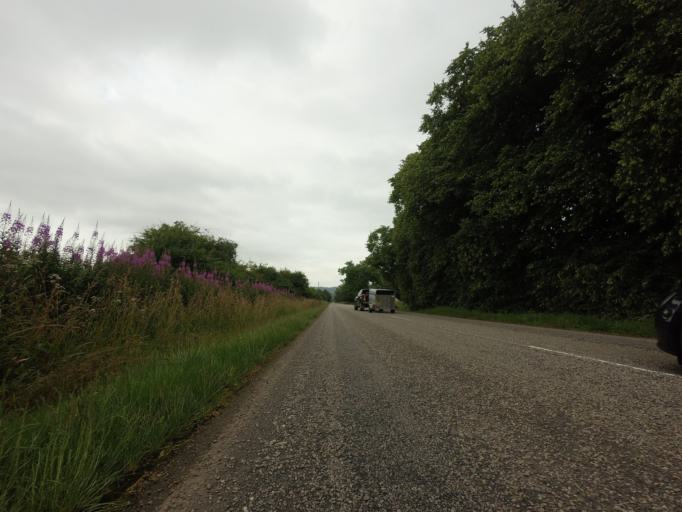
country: GB
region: Scotland
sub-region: Highland
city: Alness
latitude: 57.9129
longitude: -4.3792
